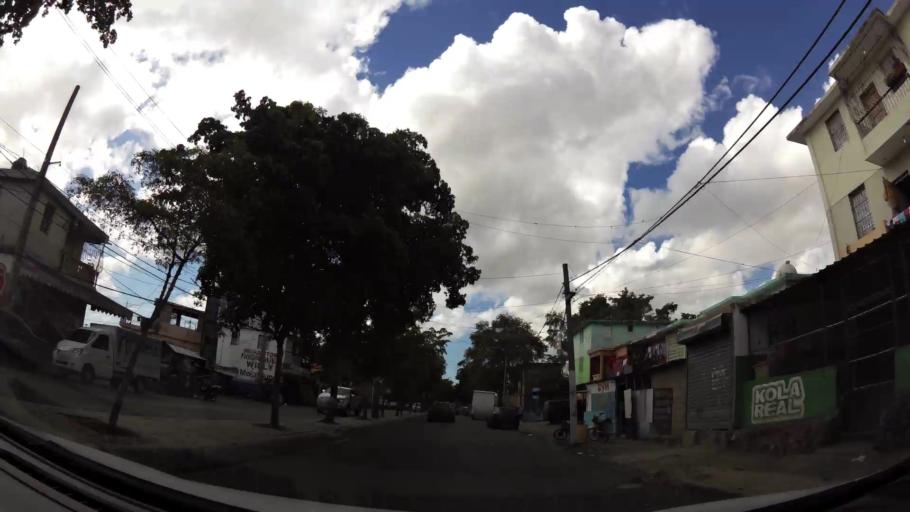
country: DO
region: Nacional
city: Ensanche Luperon
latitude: 18.4967
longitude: -69.8829
